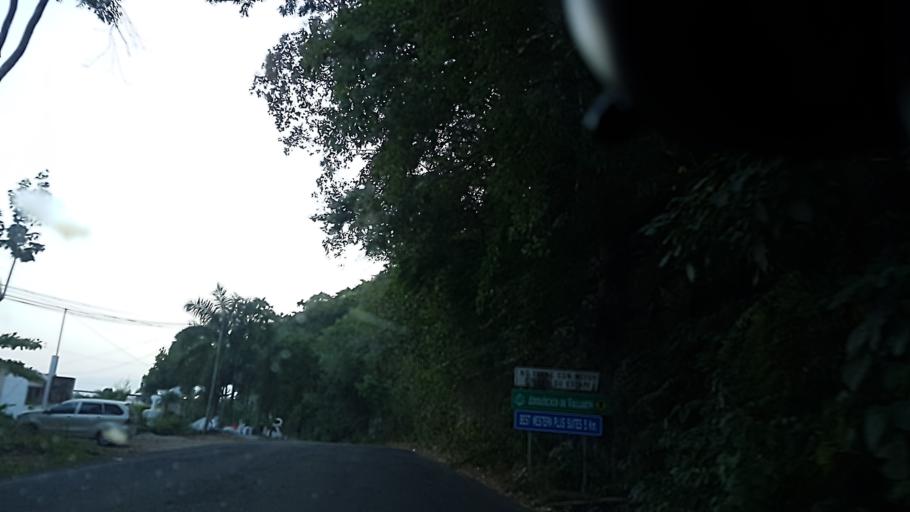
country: MX
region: Jalisco
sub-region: Puerto Vallarta
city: Puerto Vallarta
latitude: 20.5215
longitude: -105.3130
